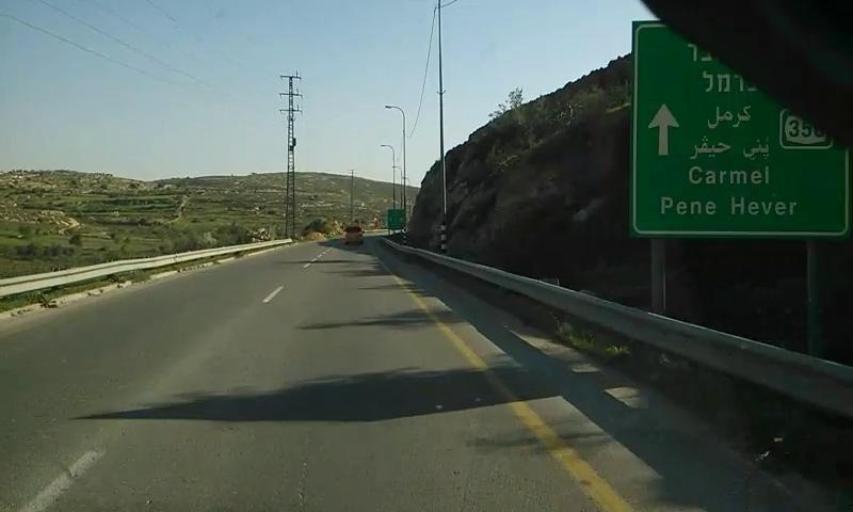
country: PS
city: Khallat ad Dar
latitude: 31.5049
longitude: 35.1336
